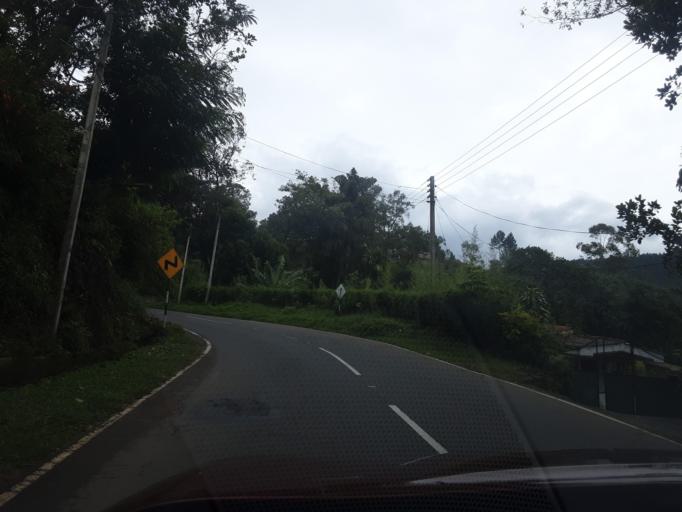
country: LK
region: Uva
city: Haputale
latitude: 6.8514
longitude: 80.9680
